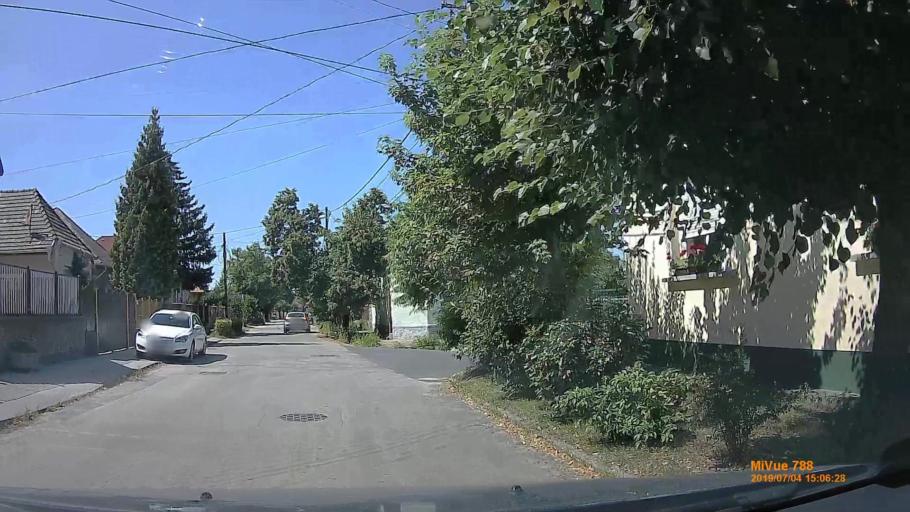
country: HU
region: Komarom-Esztergom
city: Tatabanya
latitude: 47.5711
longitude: 18.3933
